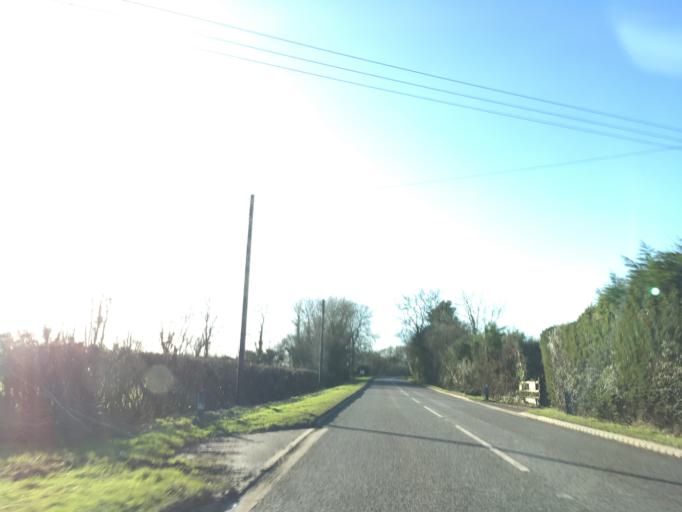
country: GB
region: England
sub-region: Wiltshire
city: Leigh
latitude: 51.6316
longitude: -1.8912
